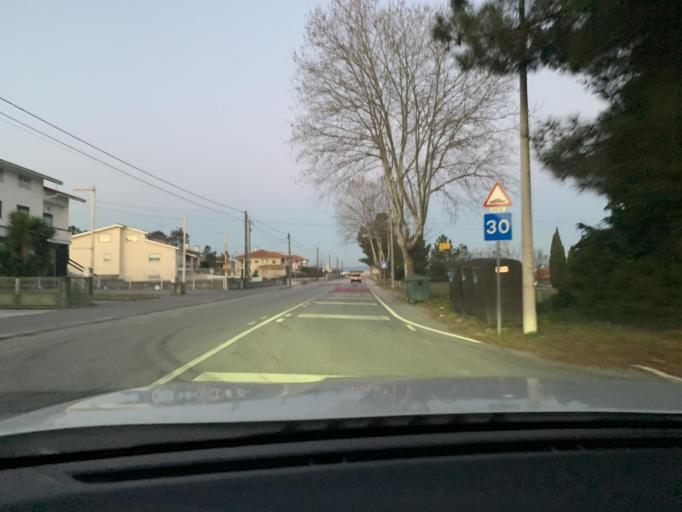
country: PT
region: Viseu
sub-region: Viseu
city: Rio de Loba
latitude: 40.6276
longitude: -7.8766
